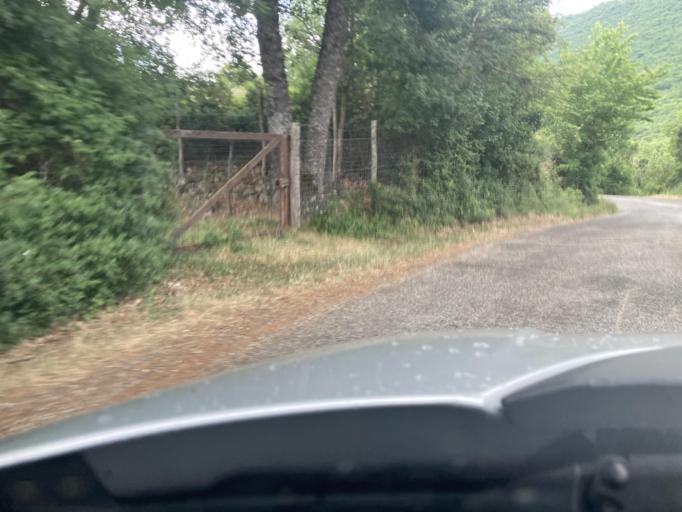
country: IT
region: Abruzzo
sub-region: Provincia dell' Aquila
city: San Panfilo d'Ocre
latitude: 42.2835
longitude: 13.4806
